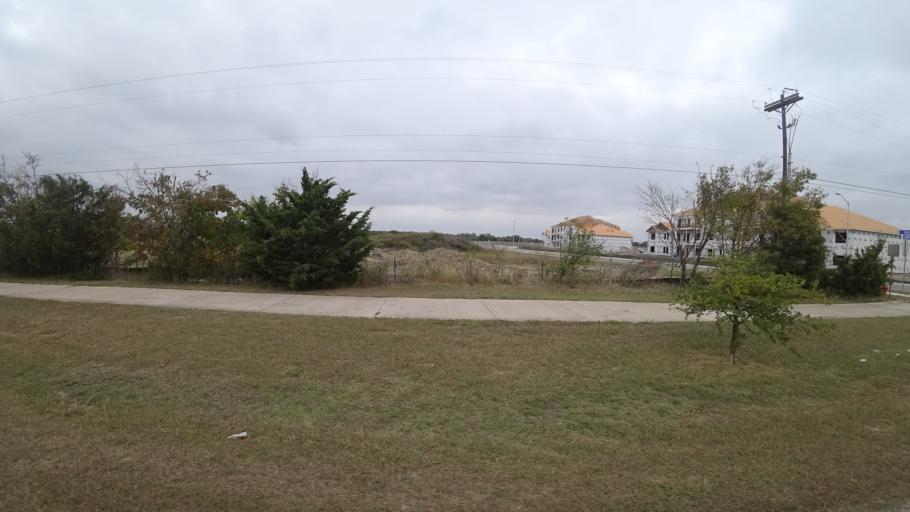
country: US
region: Texas
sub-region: Travis County
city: Pflugerville
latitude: 30.4208
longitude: -97.5936
